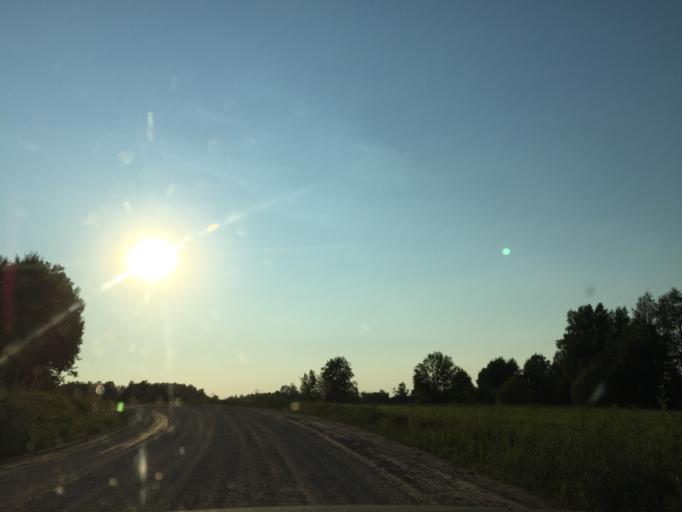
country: LV
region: Limbazu Rajons
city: Limbazi
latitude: 57.5513
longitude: 24.7819
